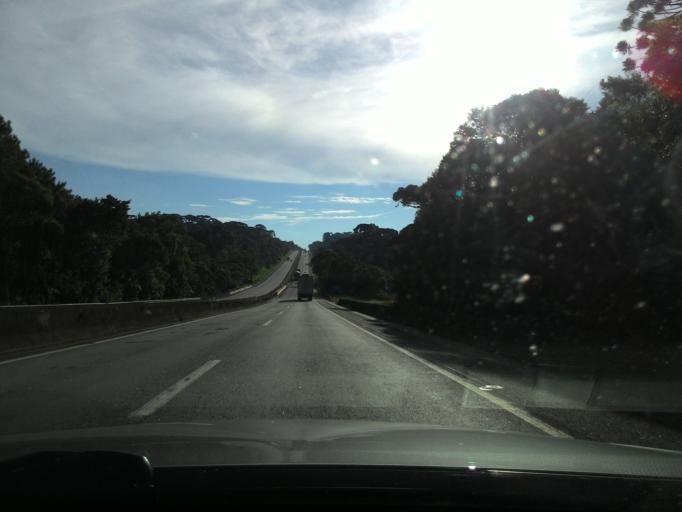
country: BR
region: Parana
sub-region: Campina Grande Do Sul
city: Campina Grande do Sul
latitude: -25.3039
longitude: -48.9678
